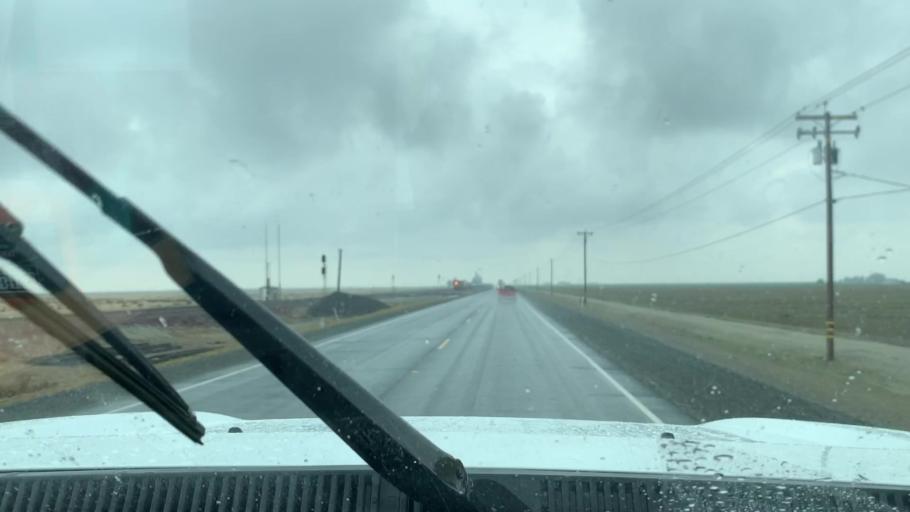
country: US
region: California
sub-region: Tulare County
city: Alpaugh
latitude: 35.9746
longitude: -119.4661
